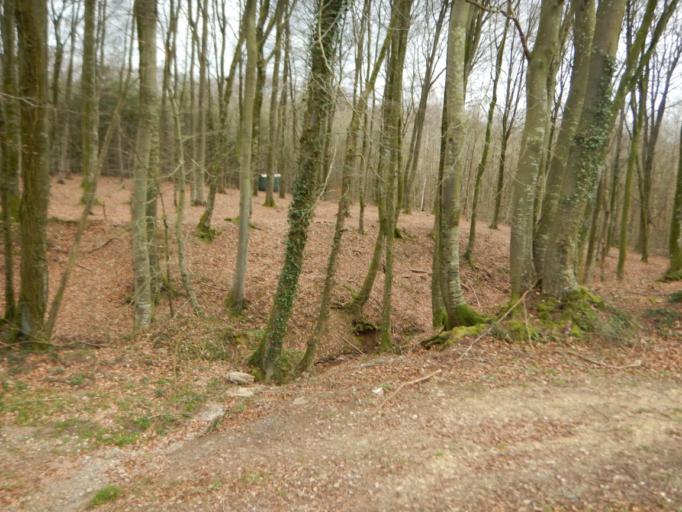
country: LU
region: Diekirch
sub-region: Canton de Redange
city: Ell
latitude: 49.7965
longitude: 5.8601
